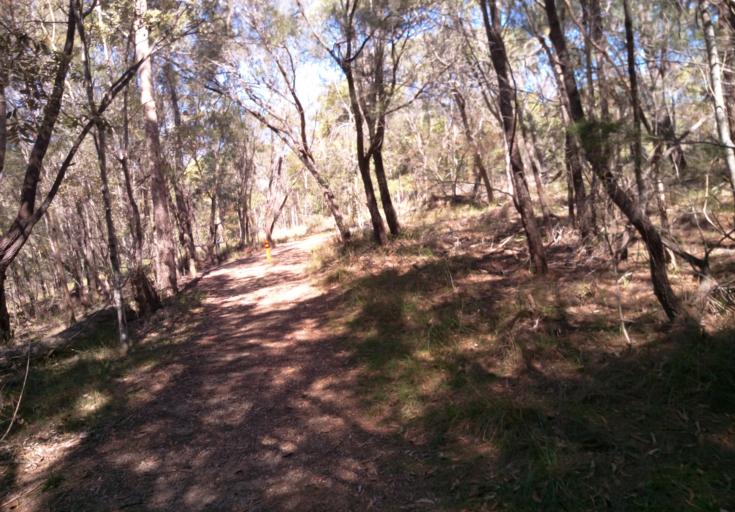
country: AU
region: Queensland
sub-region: Brisbane
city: Burbank
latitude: -27.5516
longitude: 153.2062
